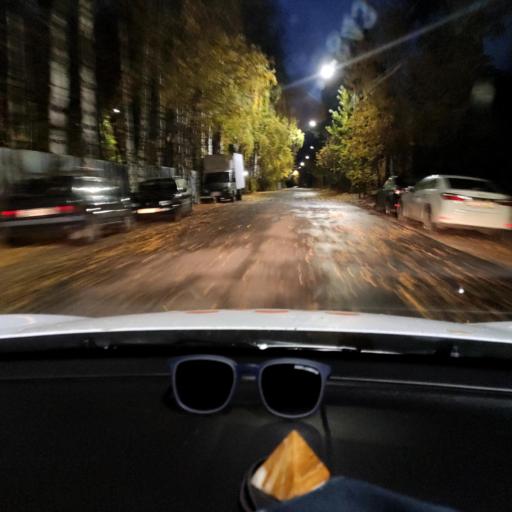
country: RU
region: Tatarstan
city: Verkhniy Uslon
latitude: 55.6000
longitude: 49.0221
